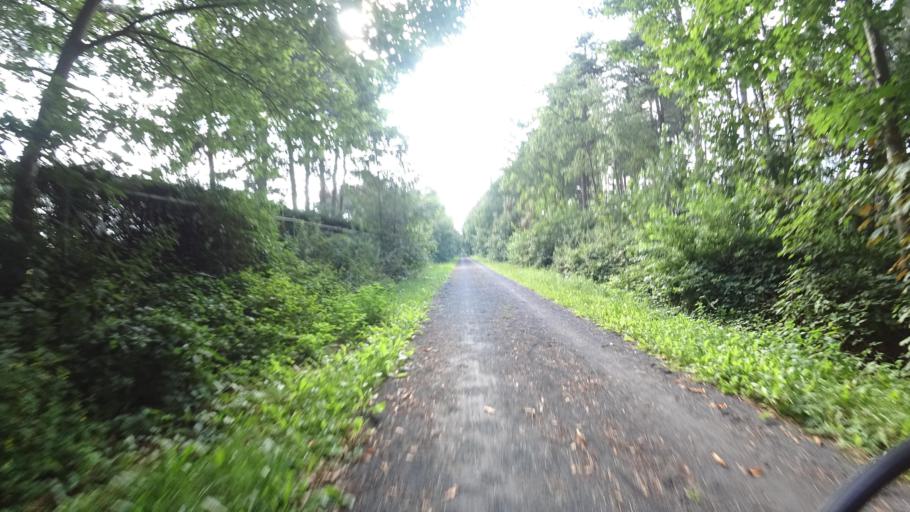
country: BE
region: Flanders
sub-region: Provincie West-Vlaanderen
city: Beernem
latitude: 51.2051
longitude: 3.3685
